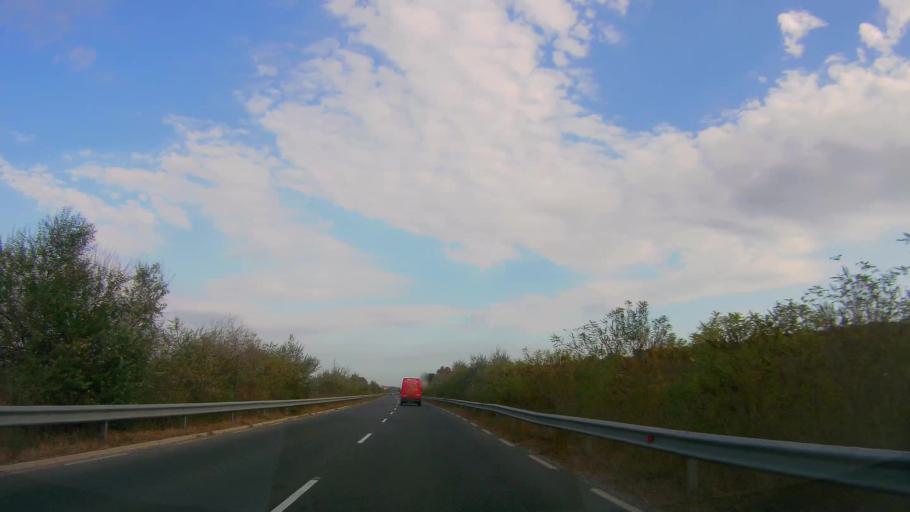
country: BG
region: Burgas
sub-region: Obshtina Sozopol
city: Sozopol
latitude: 42.3835
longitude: 27.6805
